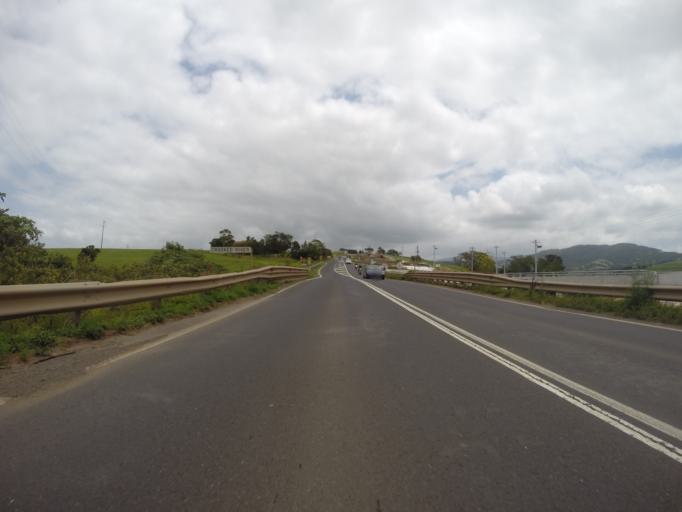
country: AU
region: New South Wales
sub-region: Kiama
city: Gerringong
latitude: -34.7457
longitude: 150.8139
